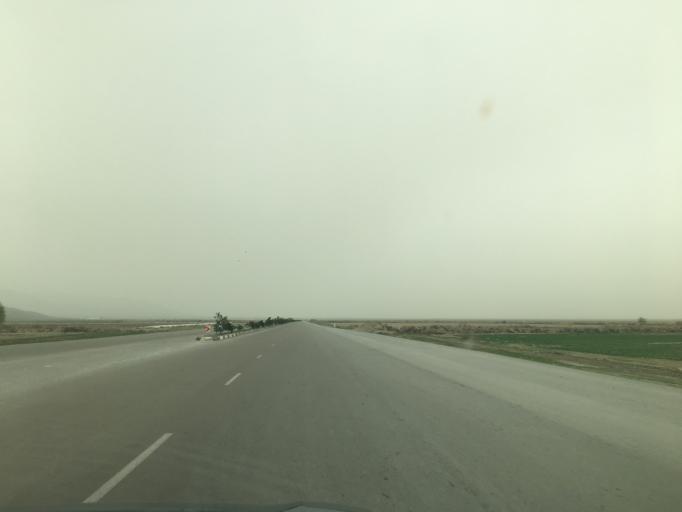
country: TM
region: Ahal
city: Baharly
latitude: 38.3297
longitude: 57.5819
